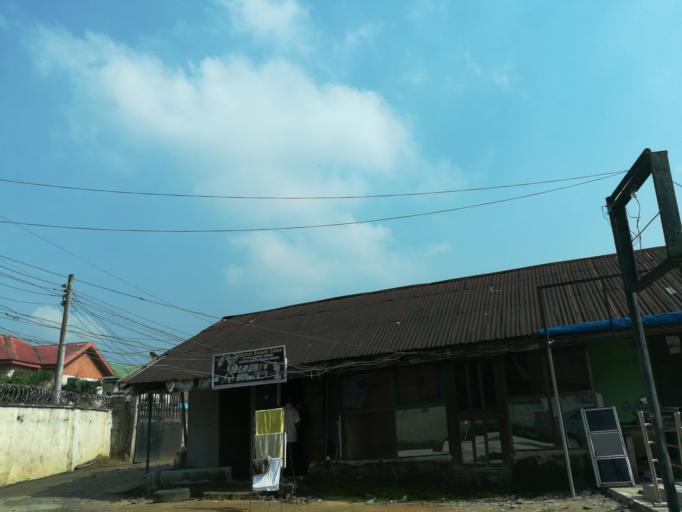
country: NG
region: Rivers
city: Port Harcourt
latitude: 4.8314
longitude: 6.9932
